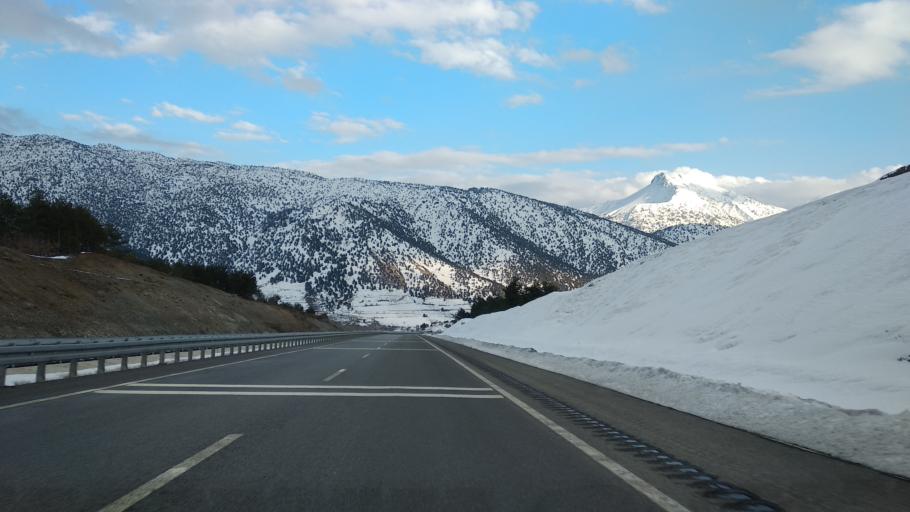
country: TR
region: Kahramanmaras
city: Goksun
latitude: 37.9050
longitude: 36.6020
